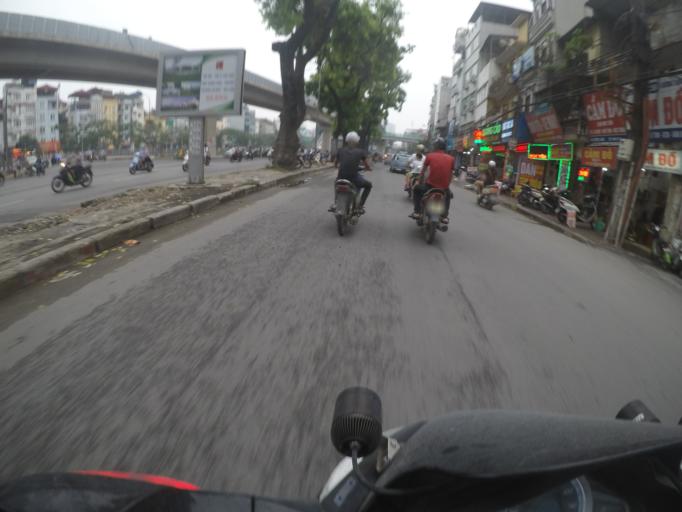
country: VN
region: Ha Noi
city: Dong Da
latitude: 21.0051
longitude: 105.8173
